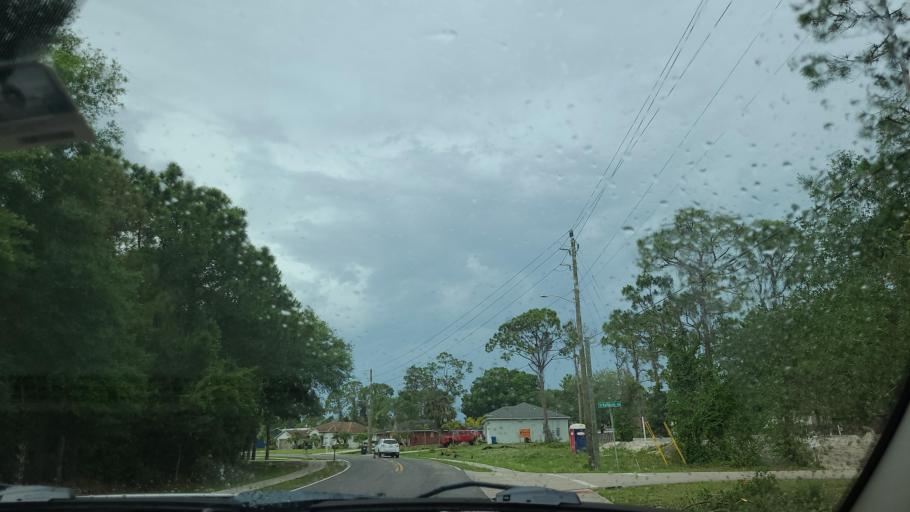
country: US
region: Florida
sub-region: Brevard County
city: Grant-Valkaria
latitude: 27.9558
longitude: -80.6445
